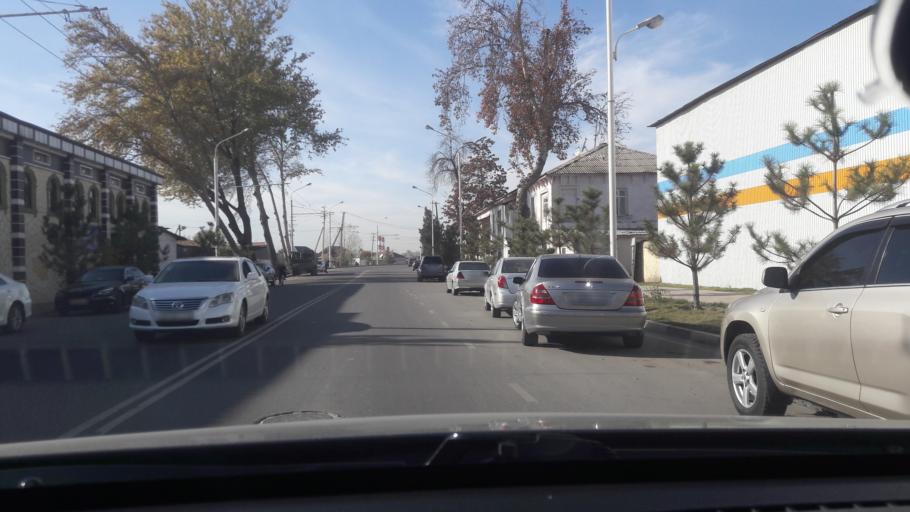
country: TJ
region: Dushanbe
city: Dushanbe
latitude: 38.5573
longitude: 68.7907
